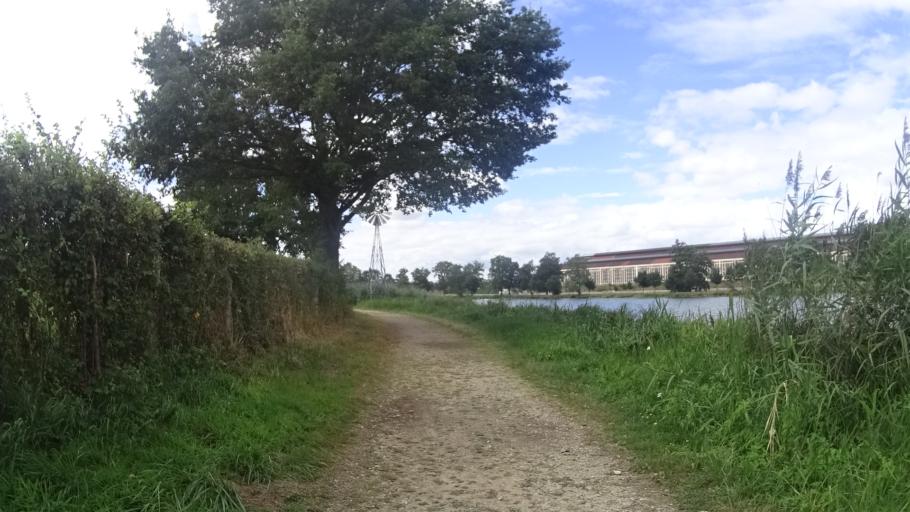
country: FR
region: Bourgogne
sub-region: Departement de Saone-et-Loire
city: Saint-Leu
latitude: 46.7420
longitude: 4.4896
